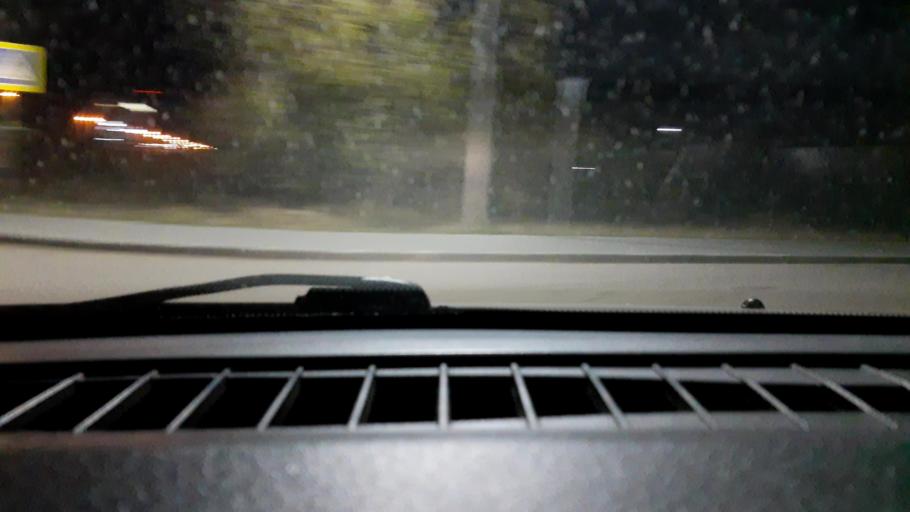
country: RU
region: Nizjnij Novgorod
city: Gorbatovka
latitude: 56.3622
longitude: 43.7935
